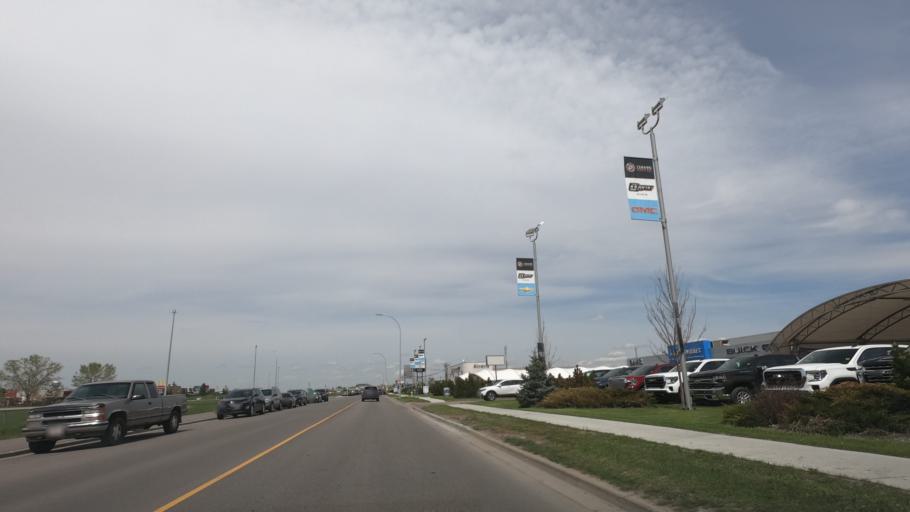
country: CA
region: Alberta
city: Airdrie
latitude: 51.2875
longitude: -113.9995
